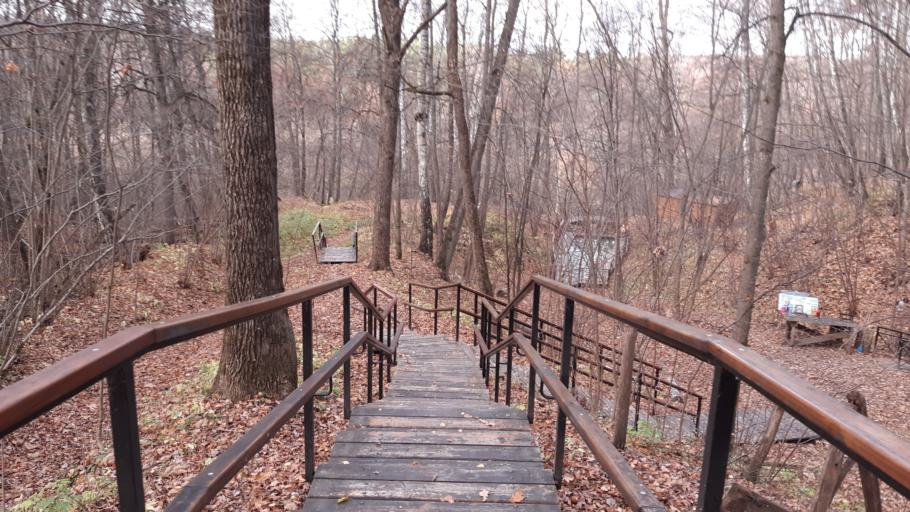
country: RU
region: Moskovskaya
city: Dubrovitsy
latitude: 55.4485
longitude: 37.4979
